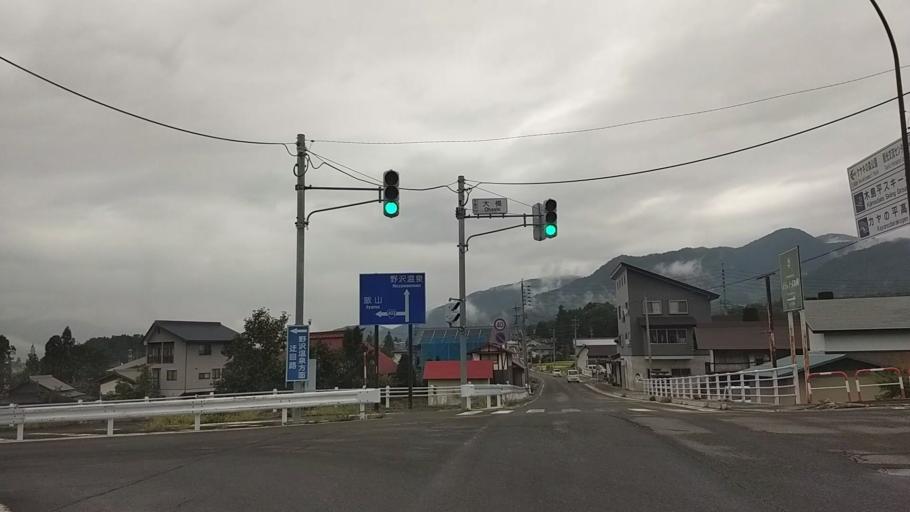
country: JP
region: Nagano
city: Iiyama
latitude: 36.8444
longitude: 138.4053
